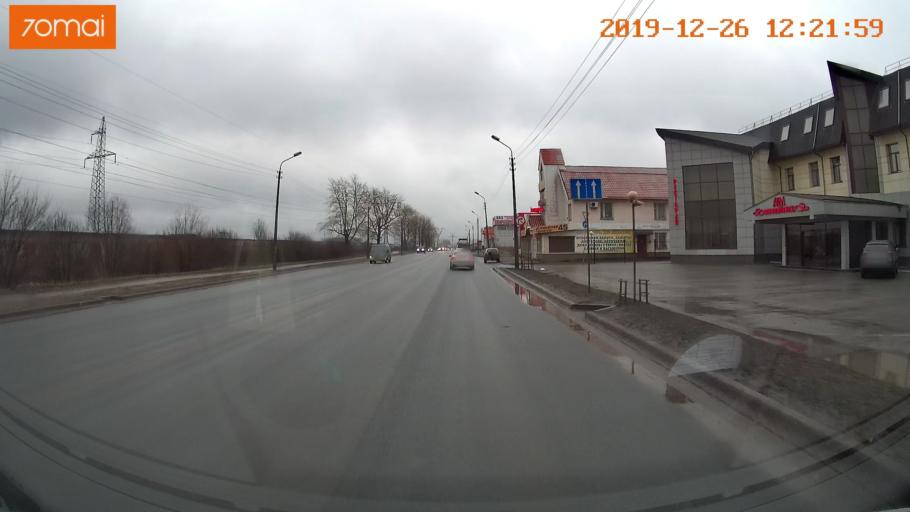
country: RU
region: Vologda
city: Cherepovets
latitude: 59.1511
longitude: 37.9390
